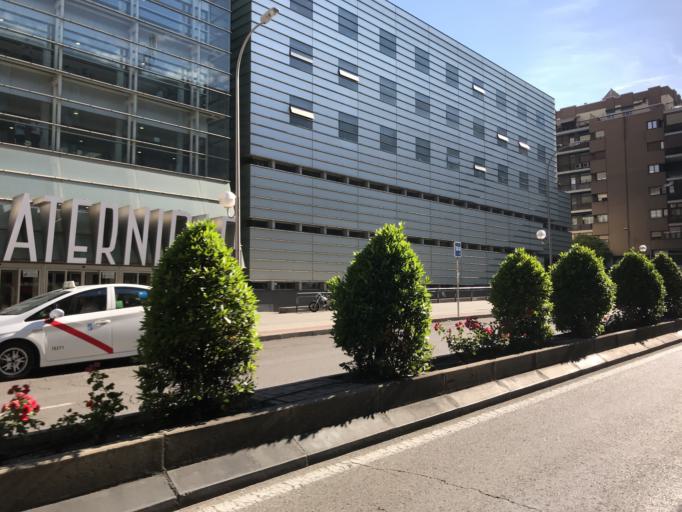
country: ES
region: Madrid
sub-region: Provincia de Madrid
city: Salamanca
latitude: 40.4213
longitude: -3.6718
